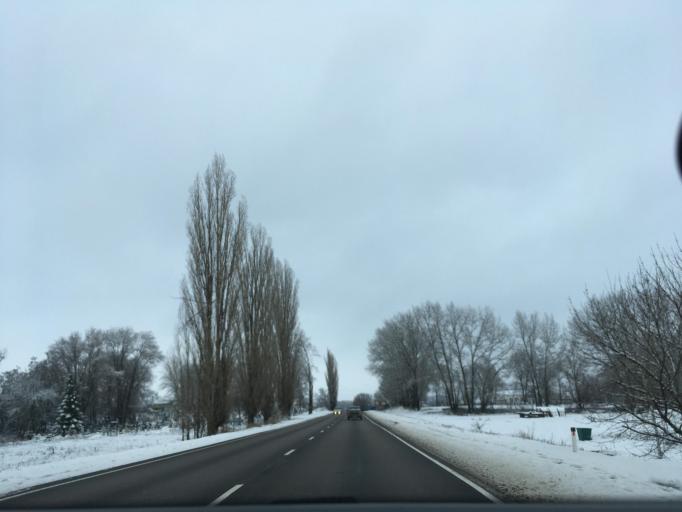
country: RU
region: Voronezj
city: Zabolotovka
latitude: 50.2467
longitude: 39.3662
